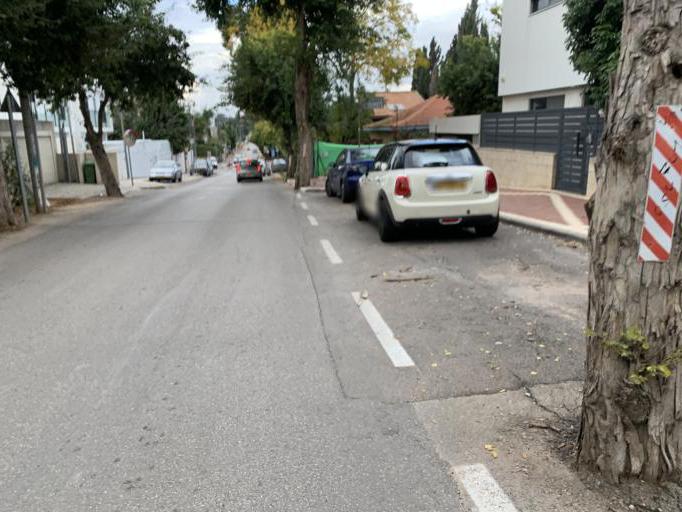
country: IL
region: Central District
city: Hod HaSharon
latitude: 32.1579
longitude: 34.8870
